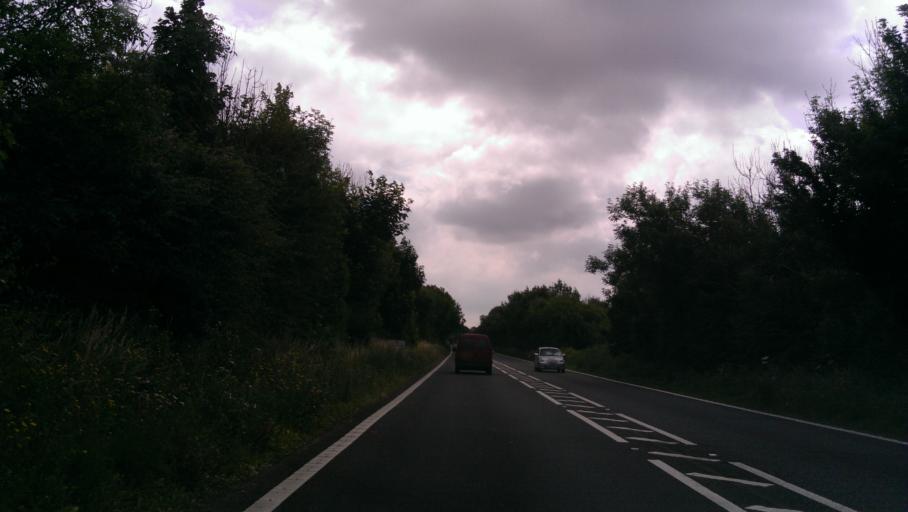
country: GB
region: England
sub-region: Kent
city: Dover
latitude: 51.1586
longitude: 1.2757
